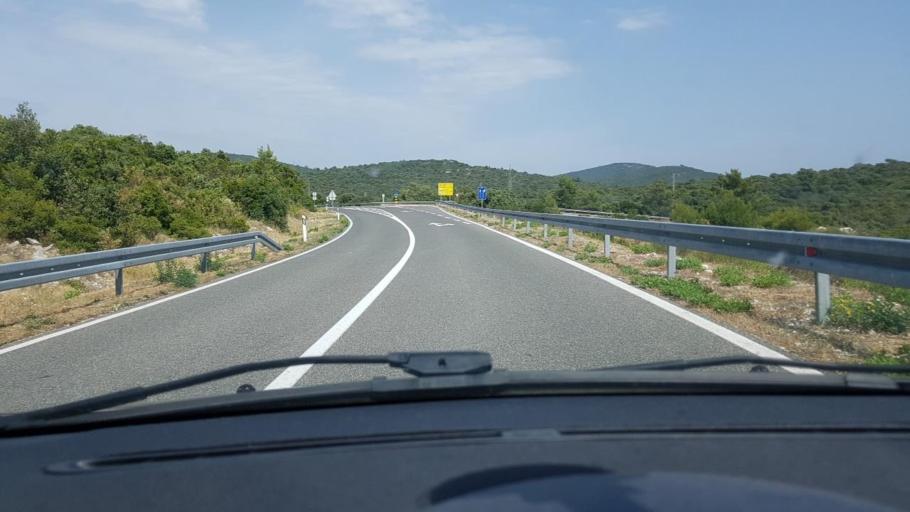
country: HR
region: Dubrovacko-Neretvanska
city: Smokvica
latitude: 42.9442
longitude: 16.9580
